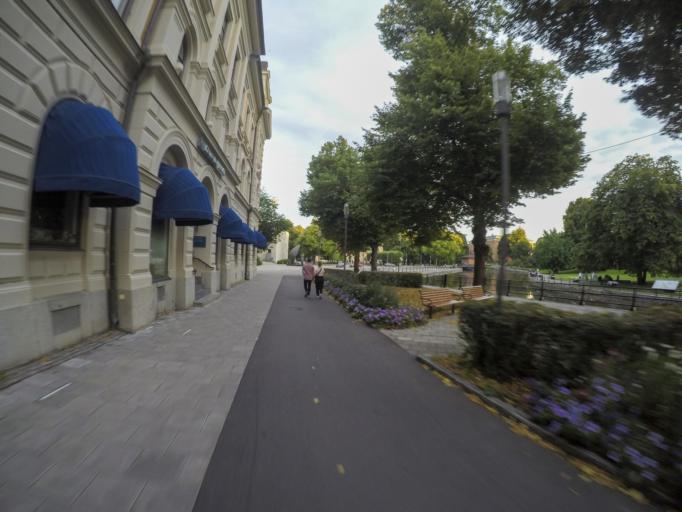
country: SE
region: Vaestmanland
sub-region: Vasteras
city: Vasteras
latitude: 59.6087
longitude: 16.5448
